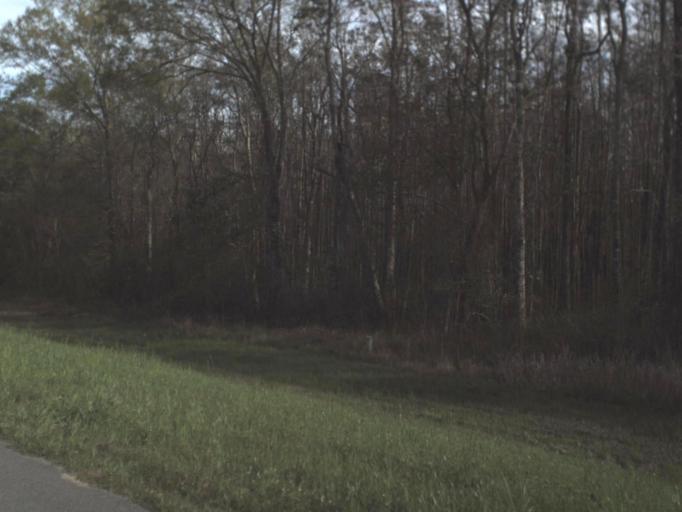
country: US
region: Florida
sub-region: Holmes County
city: Bonifay
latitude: 30.7905
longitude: -85.7057
